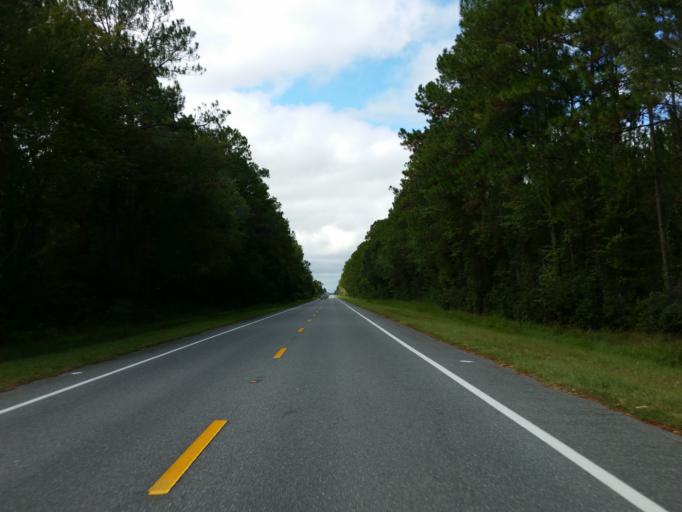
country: US
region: Florida
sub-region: Columbia County
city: Watertown
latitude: 30.1500
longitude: -82.5516
